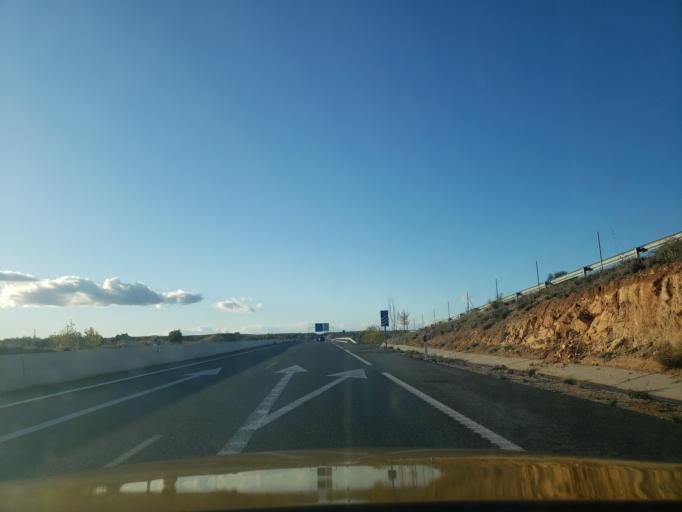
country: ES
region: Castille-La Mancha
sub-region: Province of Toledo
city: Cobisa
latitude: 39.8124
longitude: -4.0139
